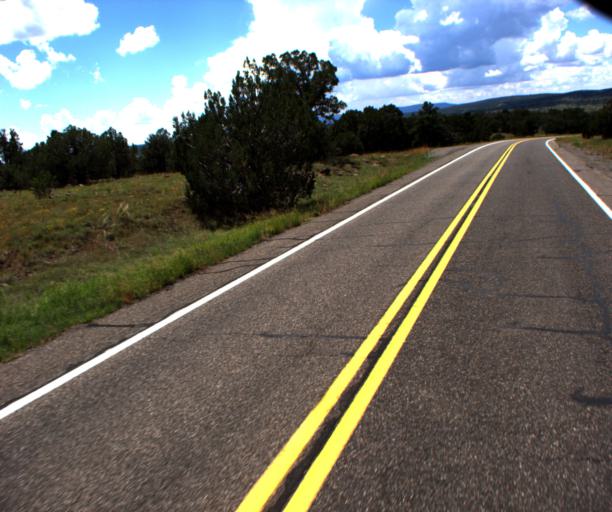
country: US
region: Arizona
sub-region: Gila County
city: Pine
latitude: 34.5101
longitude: -111.5511
